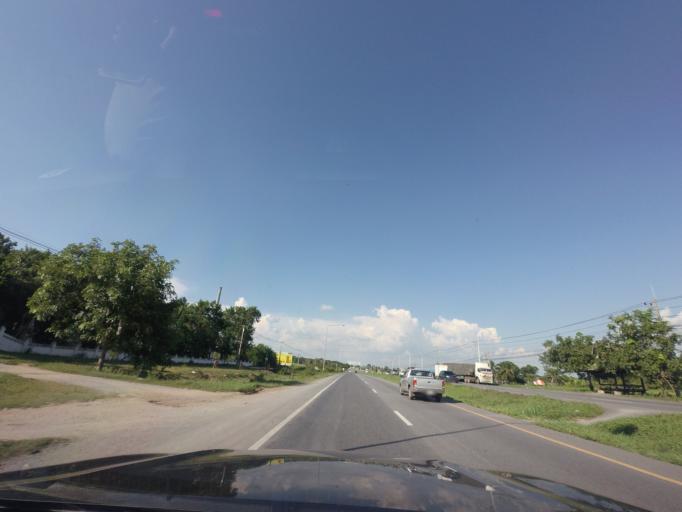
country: TH
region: Khon Kaen
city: Non Sila
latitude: 15.9524
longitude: 102.6841
